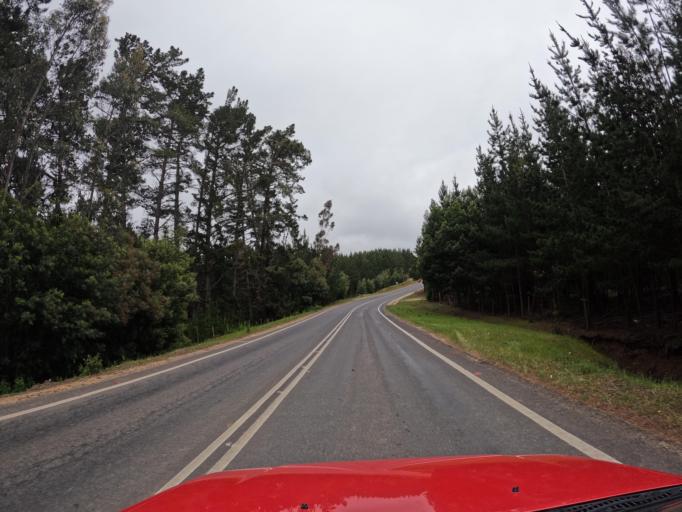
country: CL
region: O'Higgins
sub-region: Provincia de Colchagua
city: Santa Cruz
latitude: -34.5852
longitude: -72.0148
